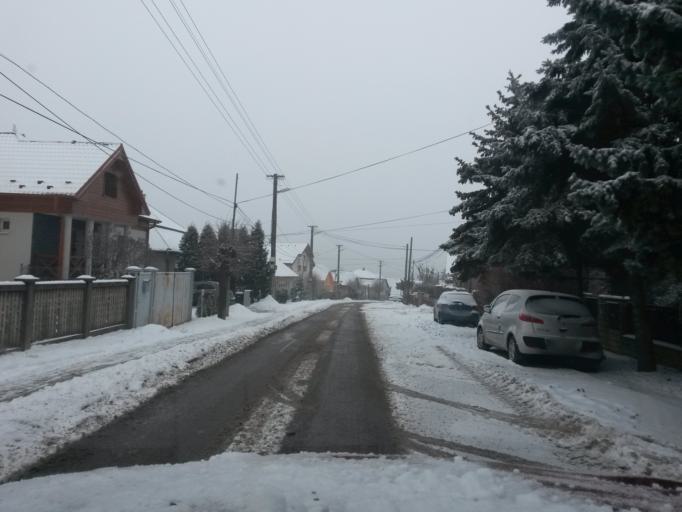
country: SK
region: Kosicky
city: Kosice
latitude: 48.7294
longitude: 21.3030
